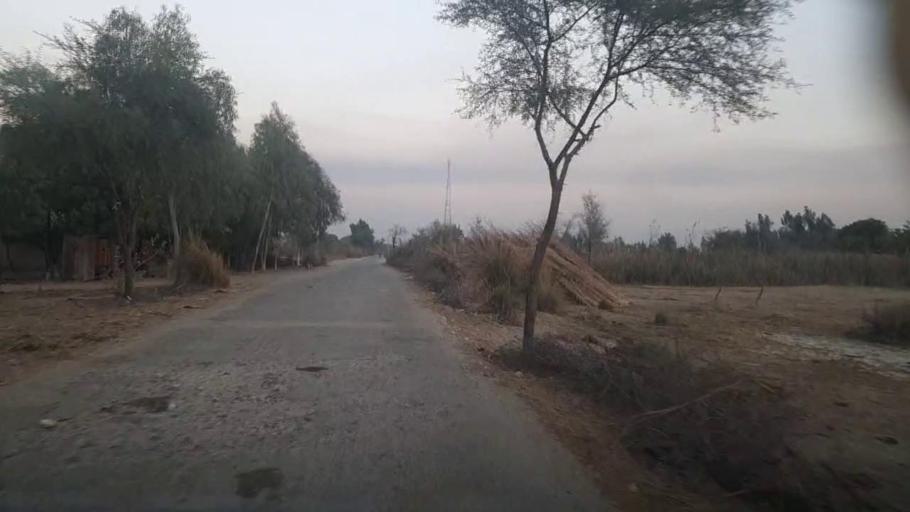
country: PK
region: Sindh
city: Kandiari
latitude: 26.6850
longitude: 68.9331
